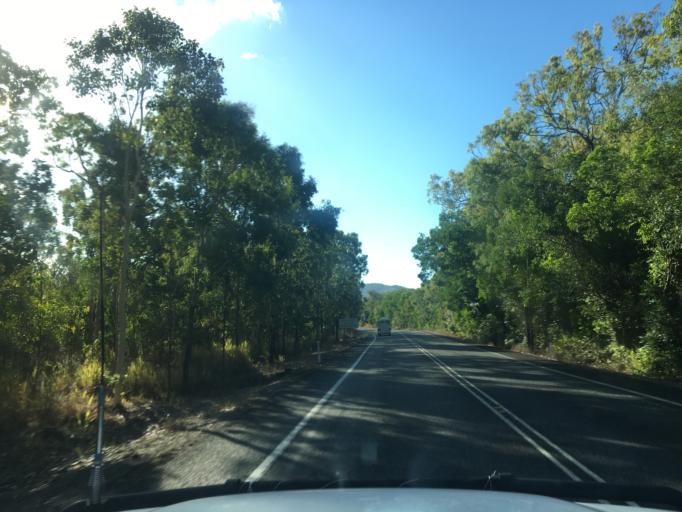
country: AU
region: Queensland
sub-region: Cairns
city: Palm Cove
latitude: -16.6821
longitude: 145.5751
